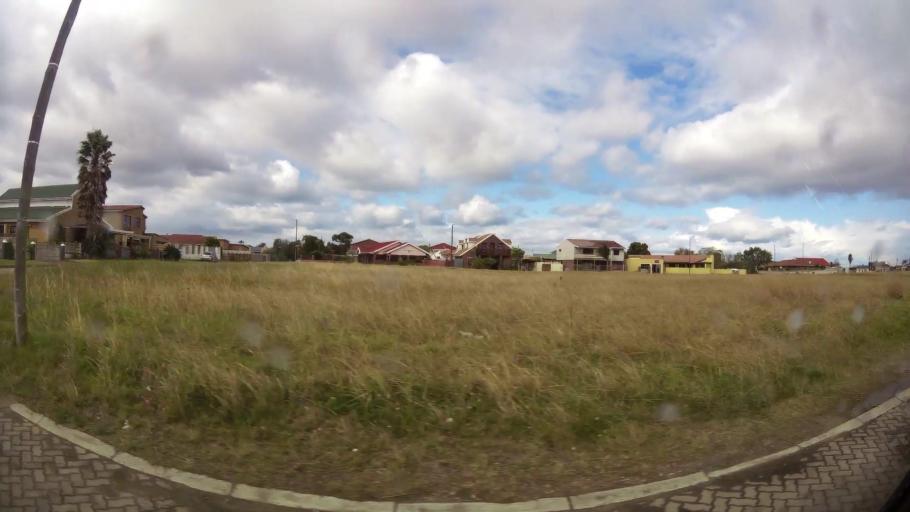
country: ZA
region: Western Cape
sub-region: Eden District Municipality
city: George
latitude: -33.9747
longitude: 22.4909
